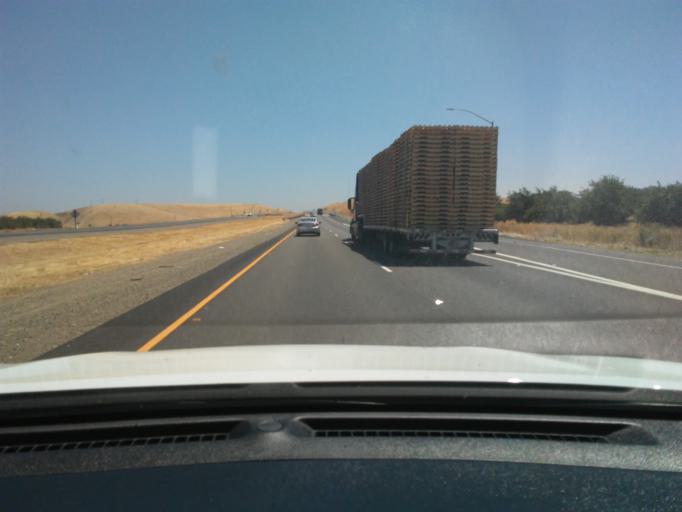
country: US
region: California
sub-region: Stanislaus County
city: Patterson
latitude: 37.3996
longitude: -121.1400
